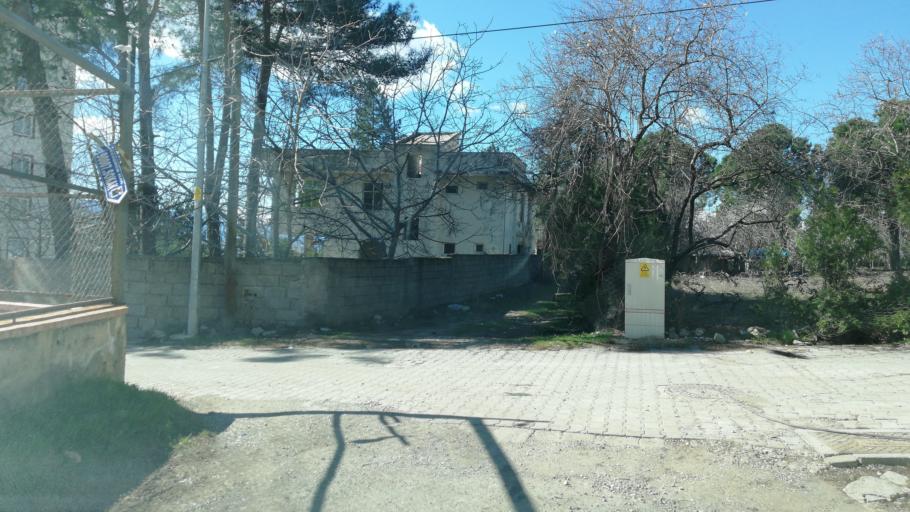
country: TR
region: Kahramanmaras
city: Kahramanmaras
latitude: 37.6011
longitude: 36.8247
